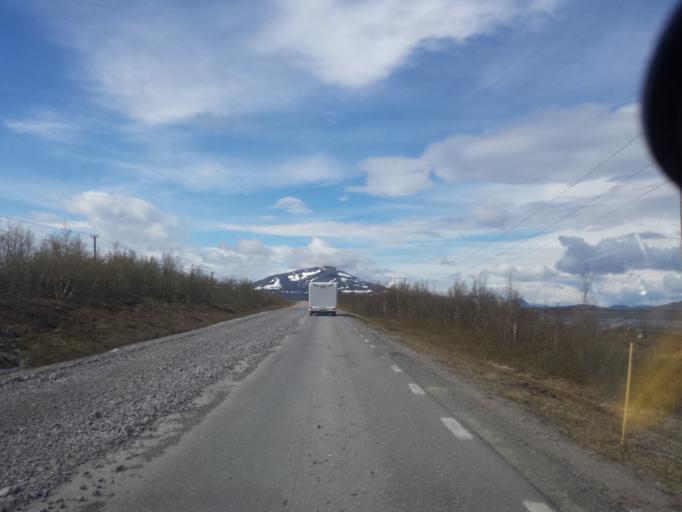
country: SE
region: Norrbotten
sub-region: Kiruna Kommun
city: Kiruna
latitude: 68.1126
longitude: 19.8326
